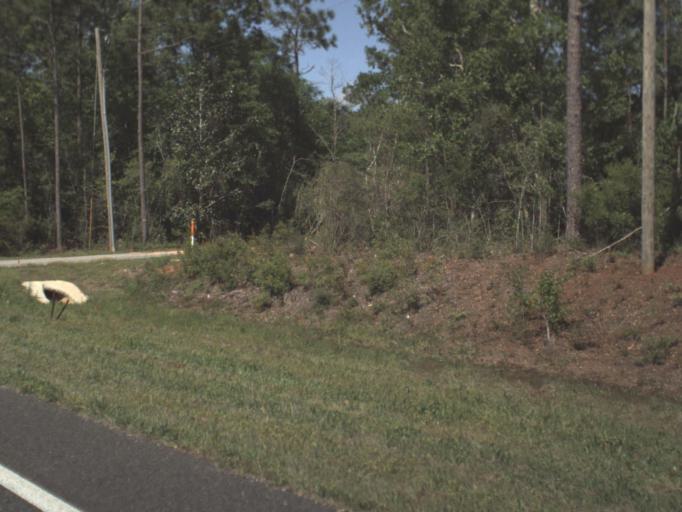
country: US
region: Florida
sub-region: Escambia County
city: Molino
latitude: 30.6758
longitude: -87.3511
